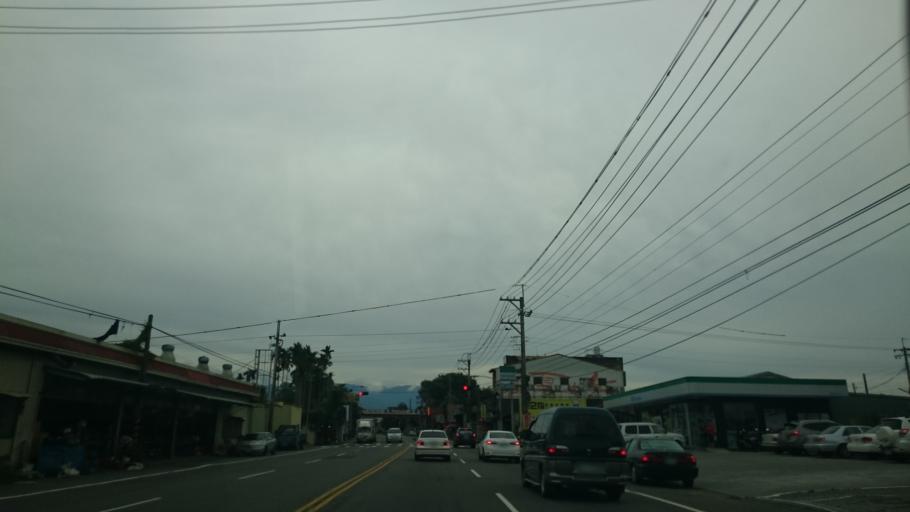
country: TW
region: Taiwan
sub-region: Nantou
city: Nantou
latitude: 23.8473
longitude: 120.6974
